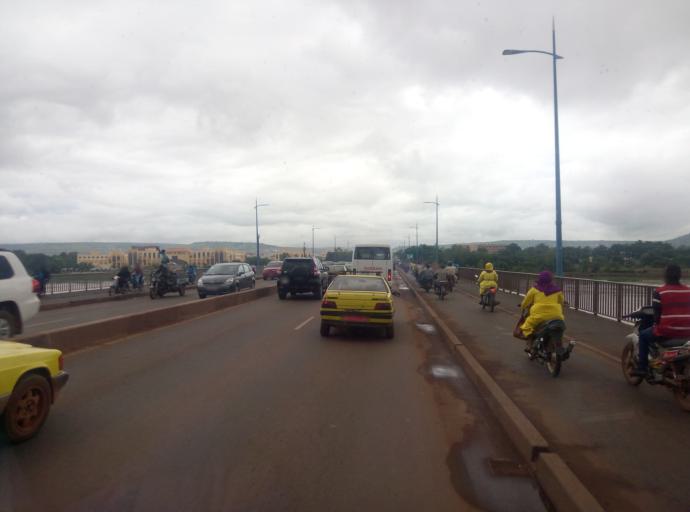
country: ML
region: Bamako
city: Bamako
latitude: 12.6245
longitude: -8.0054
